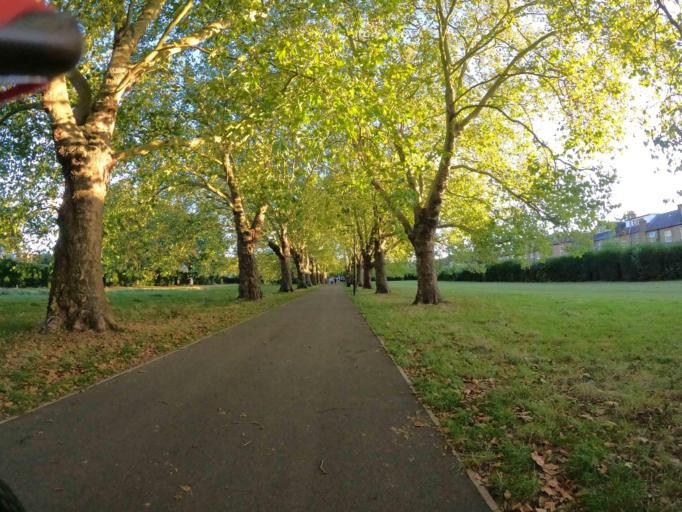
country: GB
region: England
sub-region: Greater London
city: Ealing Broadway
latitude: 51.5271
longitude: -0.3191
